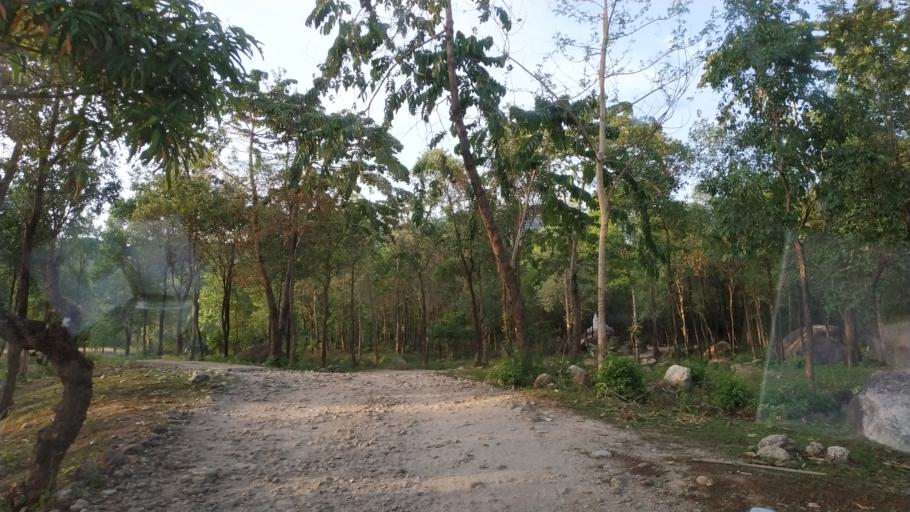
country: MM
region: Mon
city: Kyaikto
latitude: 17.4374
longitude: 97.0395
